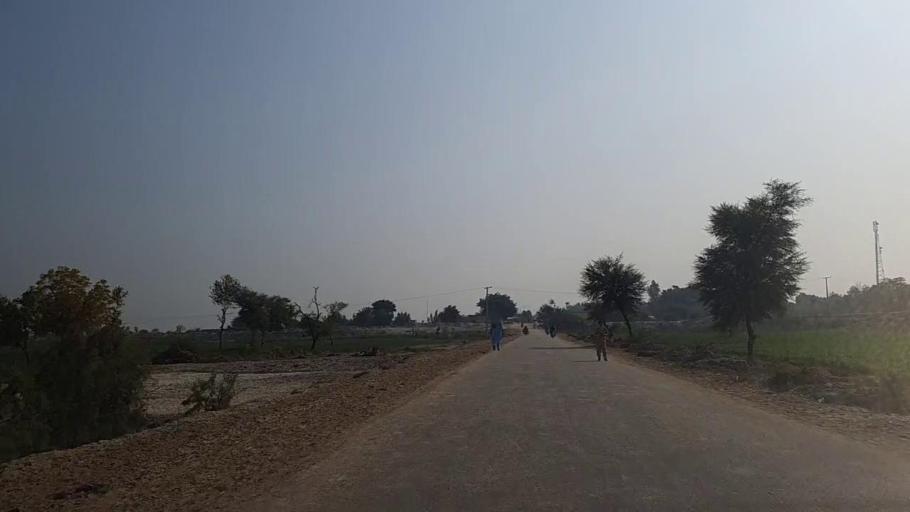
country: PK
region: Sindh
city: Jam Sahib
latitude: 26.3347
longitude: 68.5362
